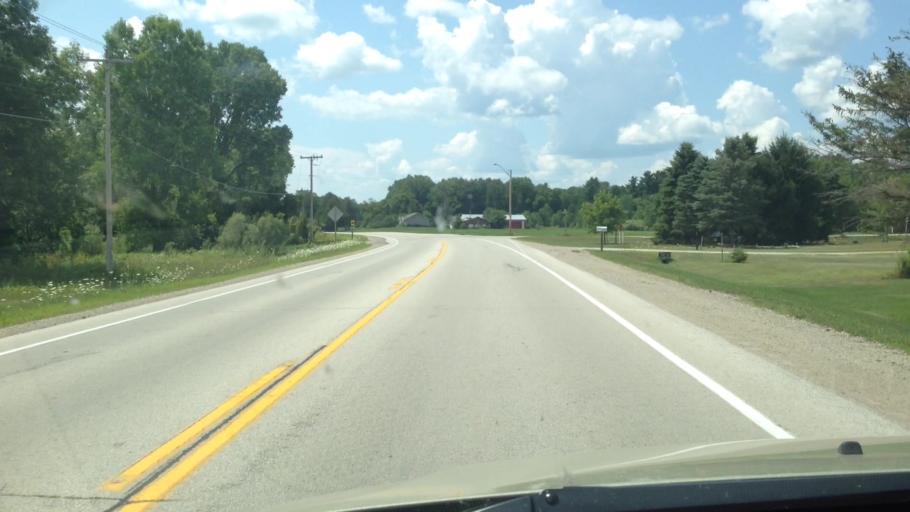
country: US
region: Wisconsin
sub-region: Brown County
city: Suamico
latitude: 44.6471
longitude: -88.1092
